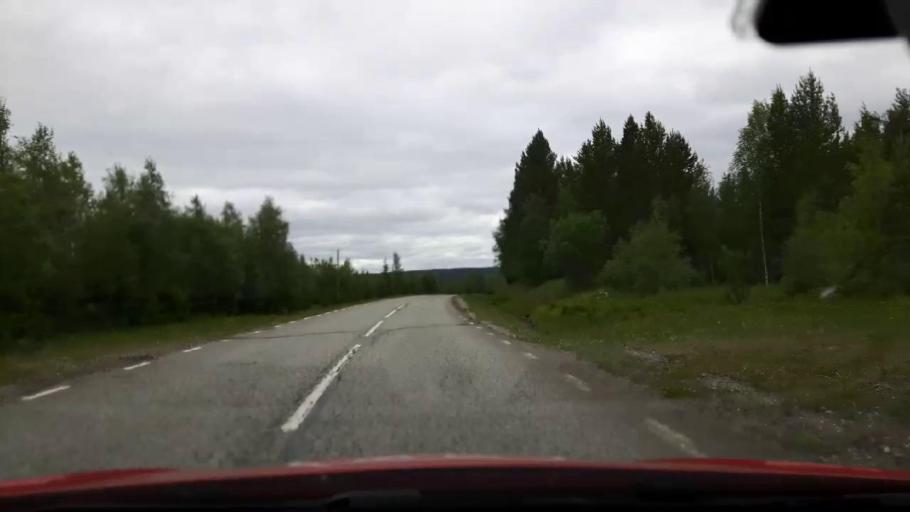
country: SE
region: Jaemtland
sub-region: Stroemsunds Kommun
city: Stroemsund
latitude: 63.3092
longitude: 15.7610
